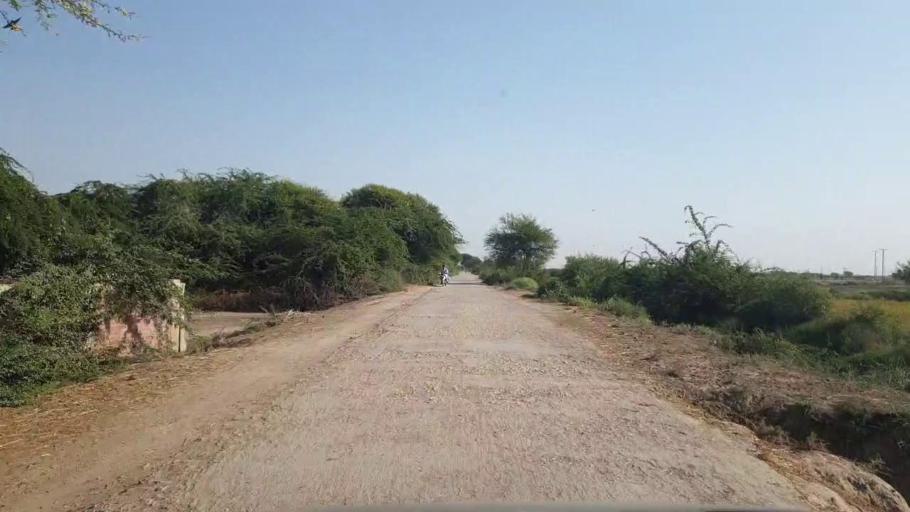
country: PK
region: Sindh
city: Matli
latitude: 25.0543
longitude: 68.7203
